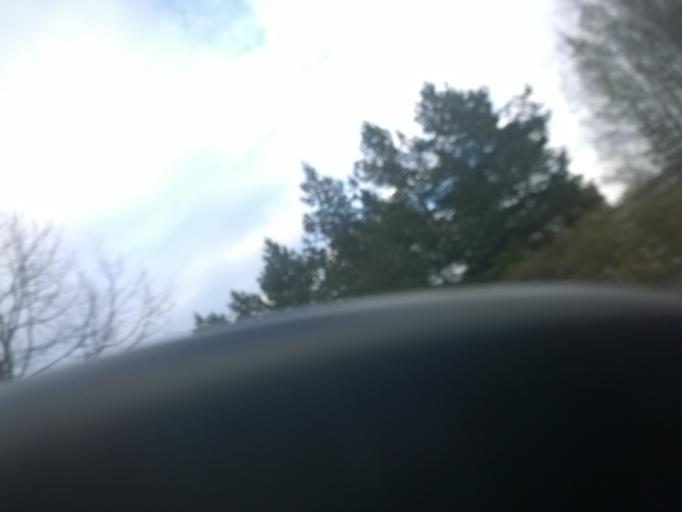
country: FI
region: Pirkanmaa
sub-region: Tampere
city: Tampere
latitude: 61.4976
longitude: 23.8162
